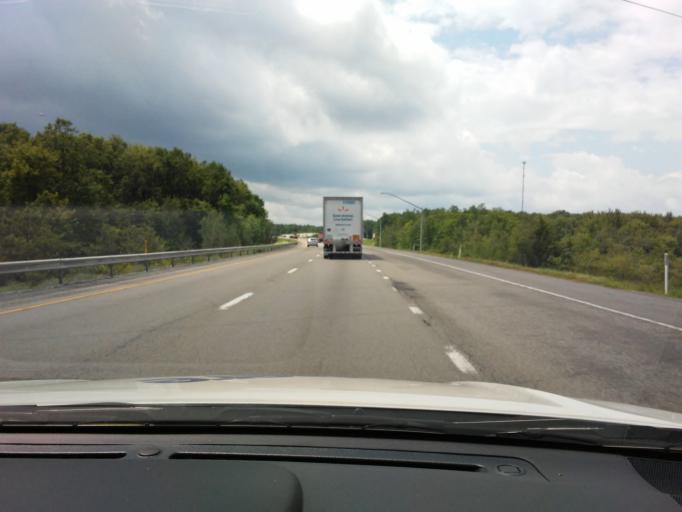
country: US
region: Pennsylvania
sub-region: Centre County
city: Milesburg
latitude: 41.0224
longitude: -77.9473
